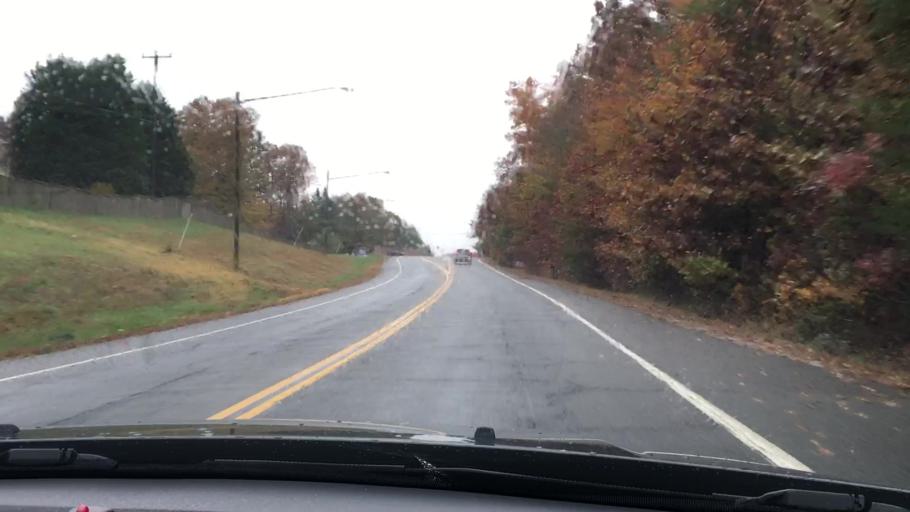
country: US
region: Virginia
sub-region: Fairfax County
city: Burke
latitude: 38.7472
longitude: -77.2829
